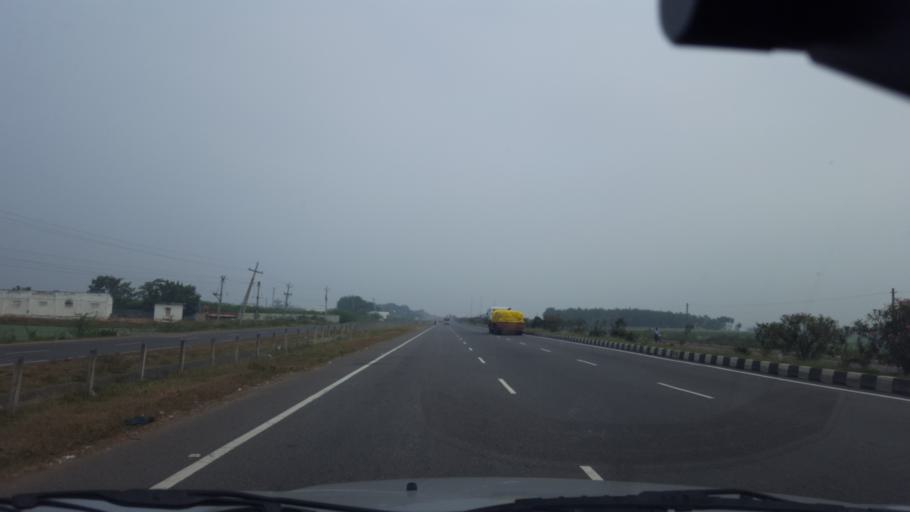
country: IN
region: Andhra Pradesh
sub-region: Guntur
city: Chilakalurupet
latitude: 16.0384
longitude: 80.1341
